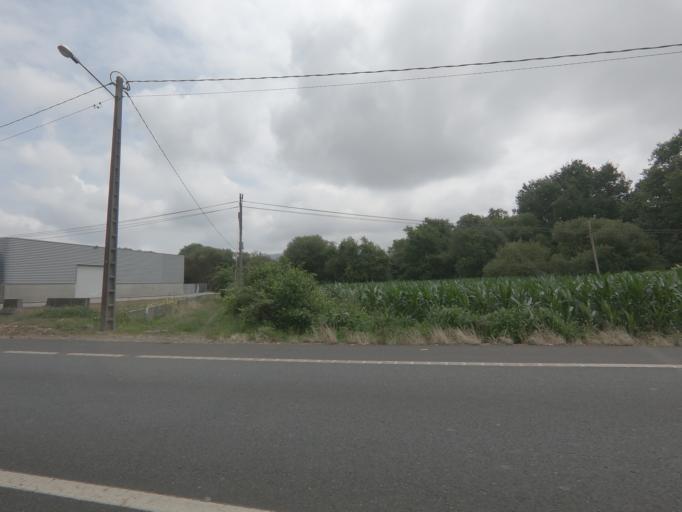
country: PT
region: Viana do Castelo
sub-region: Vila Nova de Cerveira
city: Vila Nova de Cerveira
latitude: 41.9517
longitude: -8.7688
